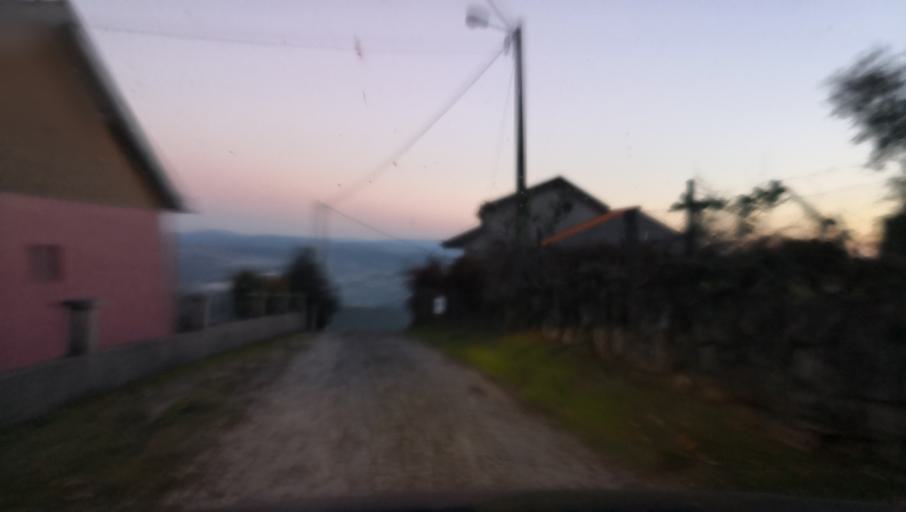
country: PT
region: Vila Real
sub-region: Vila Real
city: Vila Real
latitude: 41.3144
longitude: -7.7983
